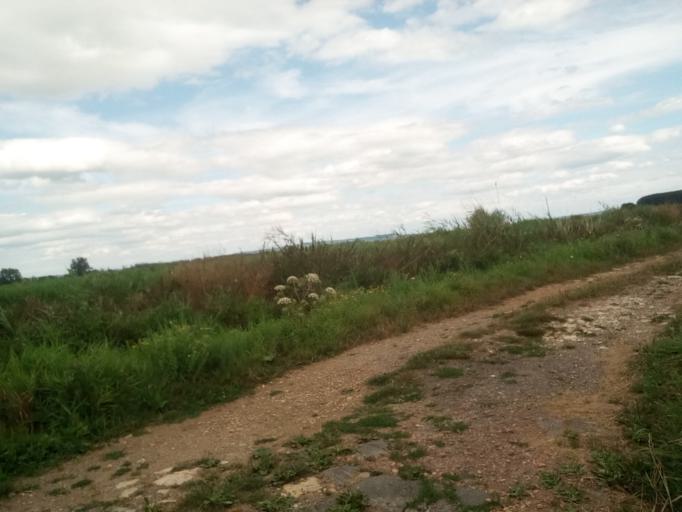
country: FR
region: Lower Normandy
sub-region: Departement du Calvados
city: Troarn
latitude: 49.1760
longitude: -0.1634
